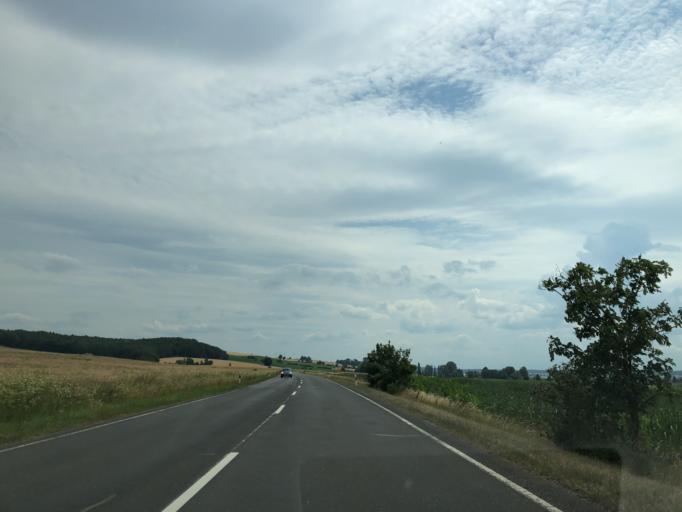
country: DE
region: Bavaria
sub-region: Regierungsbezirk Mittelfranken
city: Wachenroth
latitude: 49.7520
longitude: 10.7406
